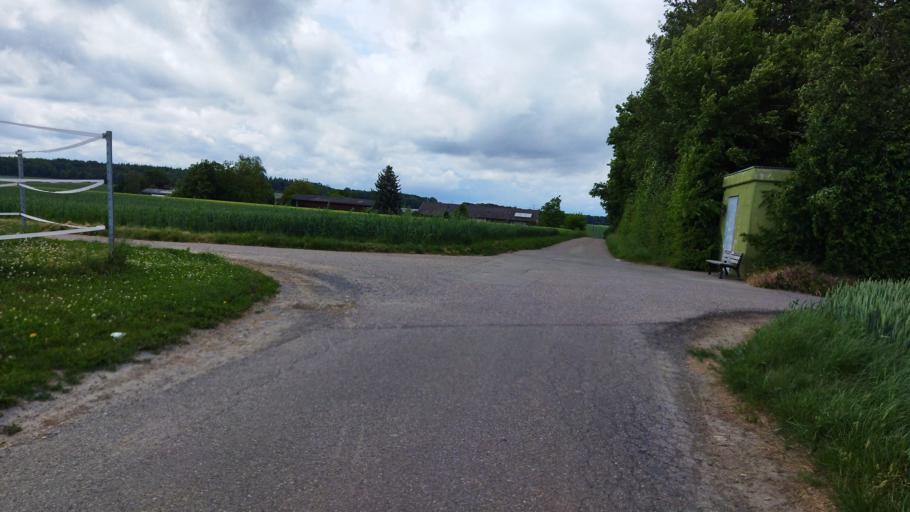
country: DE
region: Baden-Wuerttemberg
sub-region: Regierungsbezirk Stuttgart
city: Leingarten
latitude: 49.1543
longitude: 9.1221
